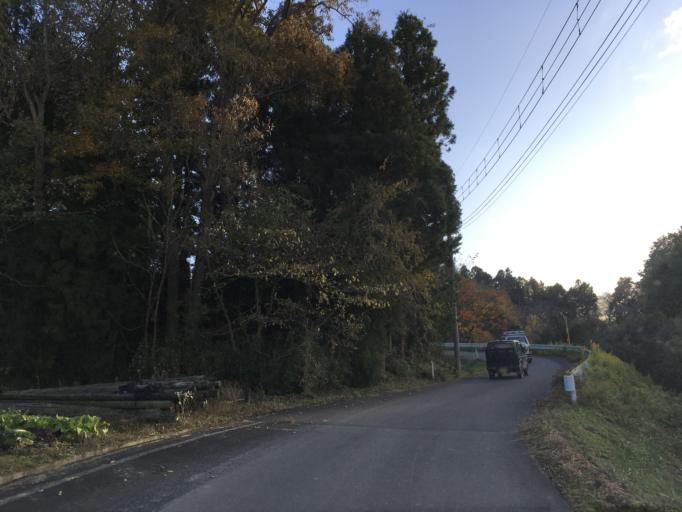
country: JP
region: Iwate
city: Ichinoseki
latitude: 38.7924
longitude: 141.1853
